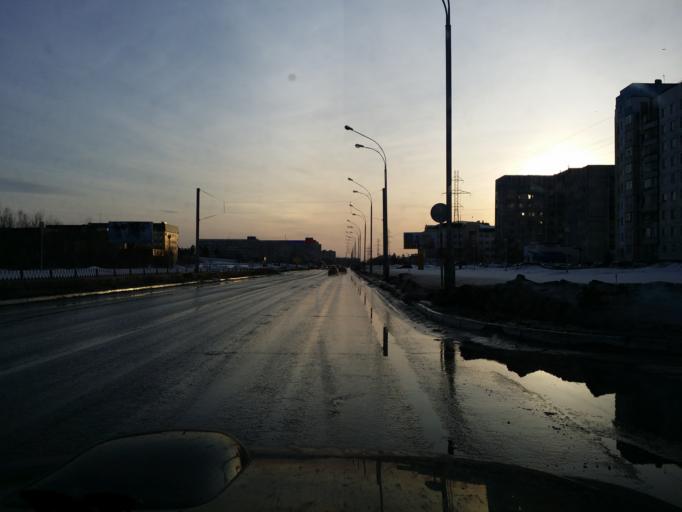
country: RU
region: Khanty-Mansiyskiy Avtonomnyy Okrug
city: Nizhnevartovsk
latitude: 60.9533
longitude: 76.5711
